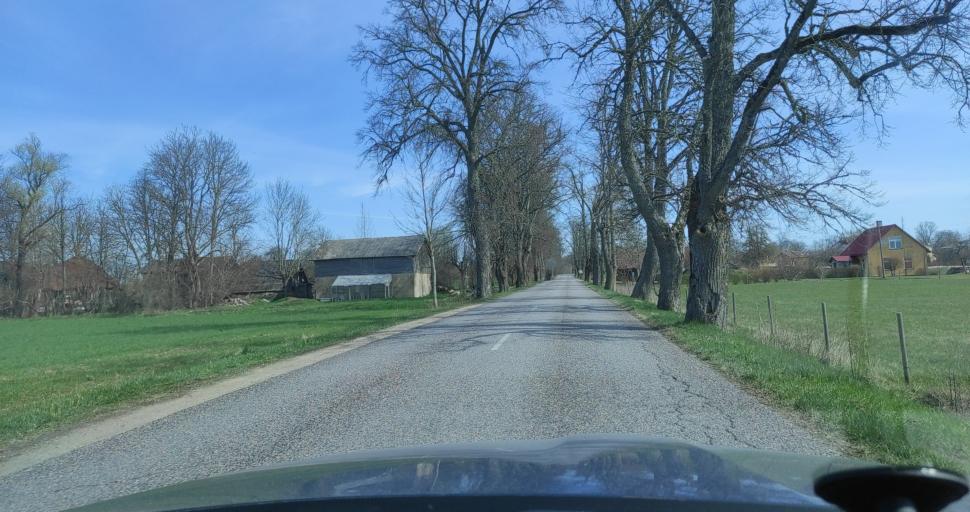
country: LV
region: Talsu Rajons
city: Stende
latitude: 57.2211
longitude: 22.5092
